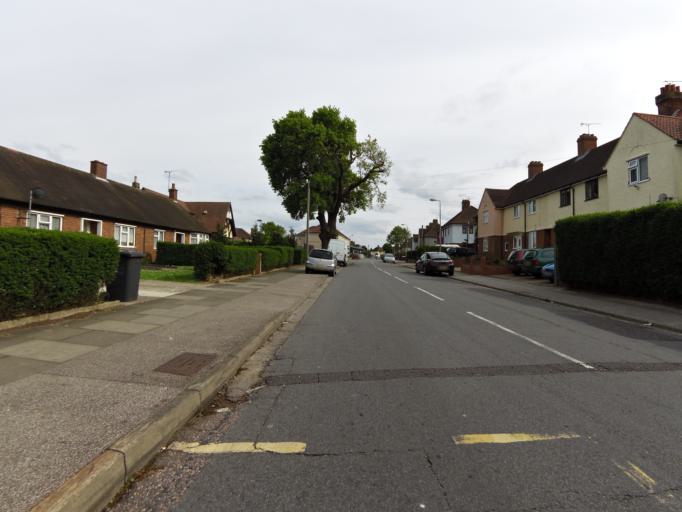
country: GB
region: England
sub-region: Suffolk
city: Ipswich
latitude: 52.0353
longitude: 1.1818
